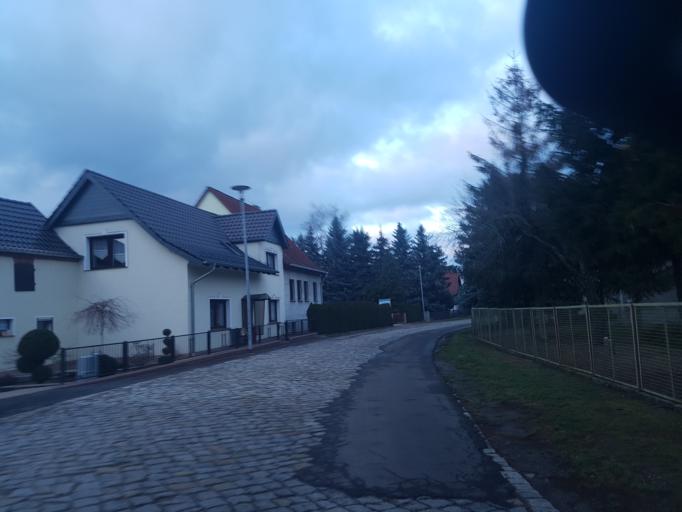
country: DE
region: Brandenburg
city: Muhlberg
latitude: 51.4675
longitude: 13.2041
